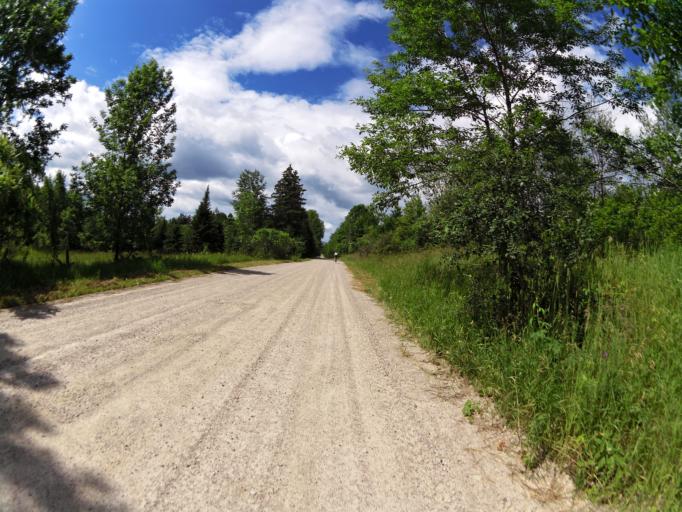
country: CA
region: Ontario
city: Perth
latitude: 45.0299
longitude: -76.5069
